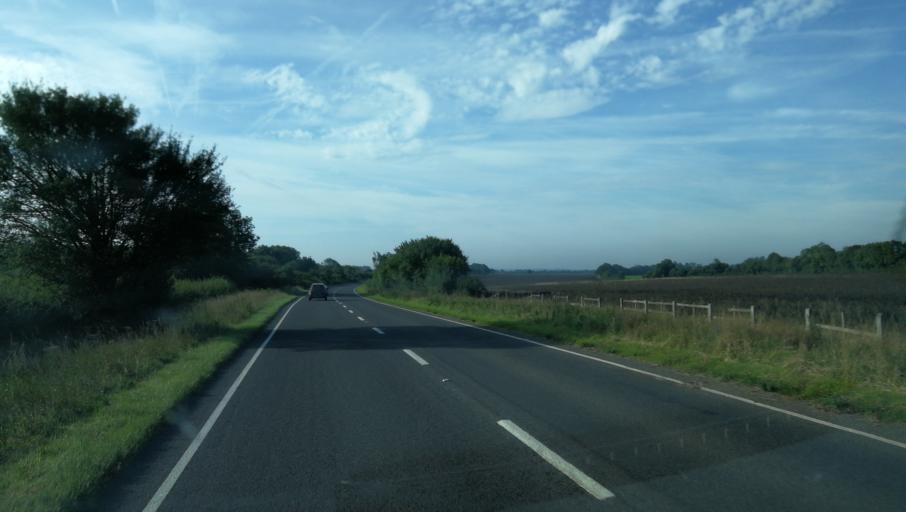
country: GB
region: England
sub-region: Oxfordshire
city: Woodstock
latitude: 51.8952
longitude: -1.3274
